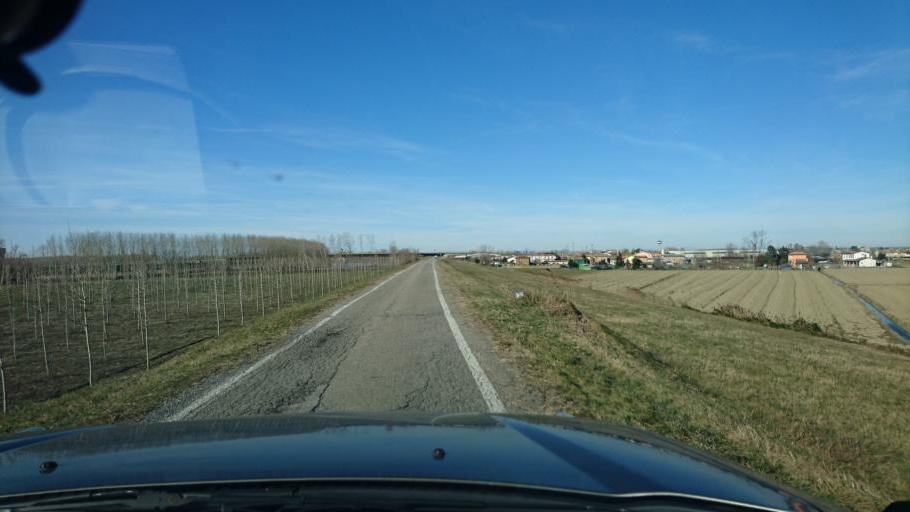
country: IT
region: Veneto
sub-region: Provincia di Rovigo
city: Ariano
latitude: 44.9355
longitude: 12.1305
